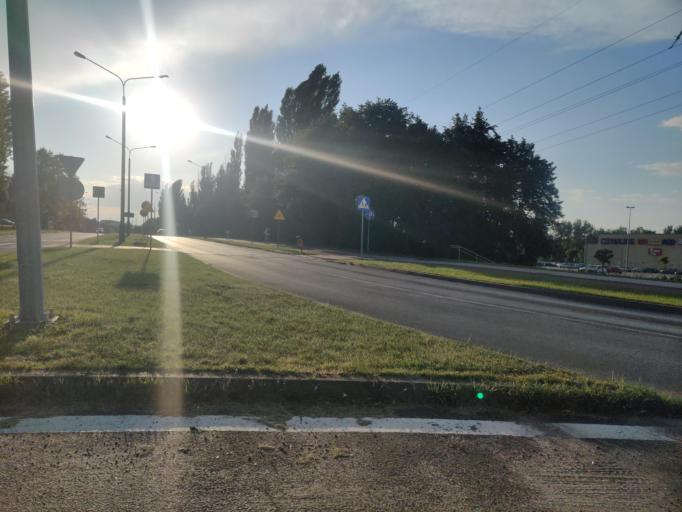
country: PL
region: Greater Poland Voivodeship
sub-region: Konin
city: Konin
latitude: 52.2368
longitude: 18.2612
